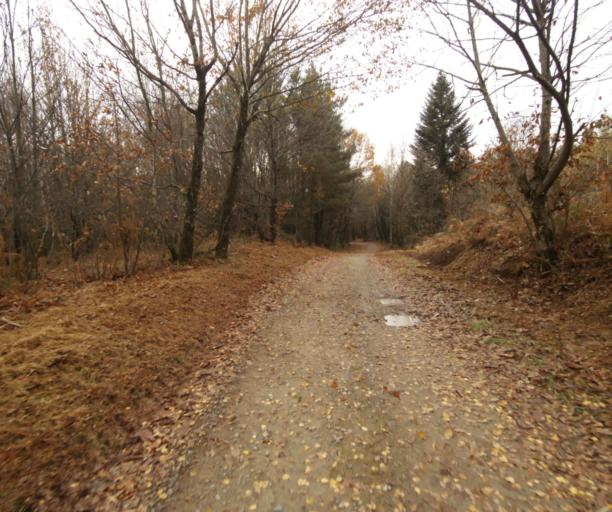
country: FR
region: Limousin
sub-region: Departement de la Correze
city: Sainte-Fortunade
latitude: 45.1909
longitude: 1.7581
